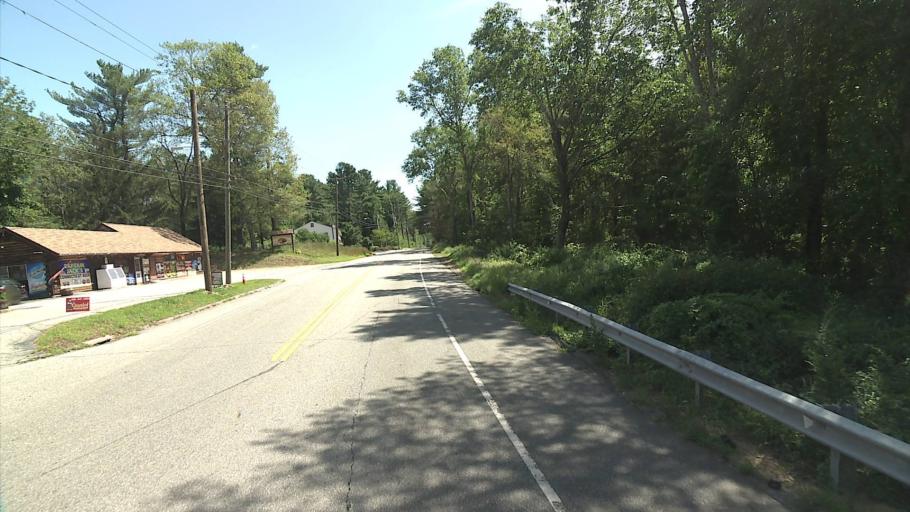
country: US
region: Connecticut
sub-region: Windham County
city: Killingly Center
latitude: 41.8498
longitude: -71.9161
